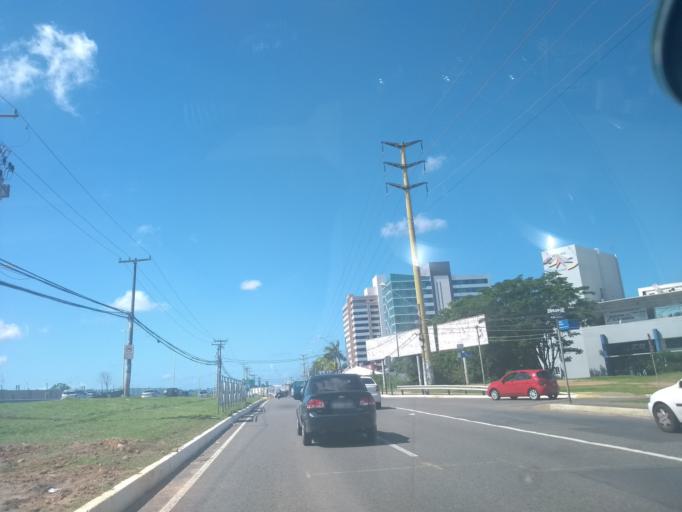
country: BR
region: Bahia
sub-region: Lauro De Freitas
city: Lauro de Freitas
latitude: -12.9384
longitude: -38.4049
